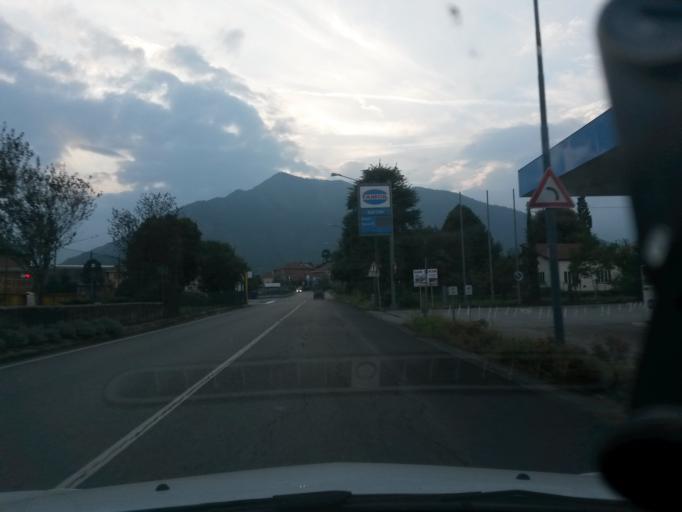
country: IT
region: Piedmont
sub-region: Provincia di Torino
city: Caselette
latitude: 45.1073
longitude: 7.4990
